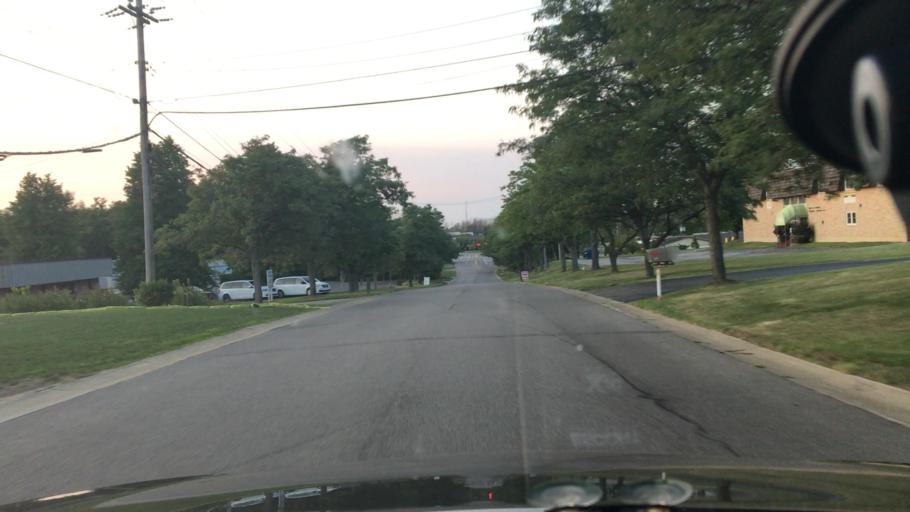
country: US
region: New York
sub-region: Erie County
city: Orchard Park
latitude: 42.7854
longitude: -78.7665
